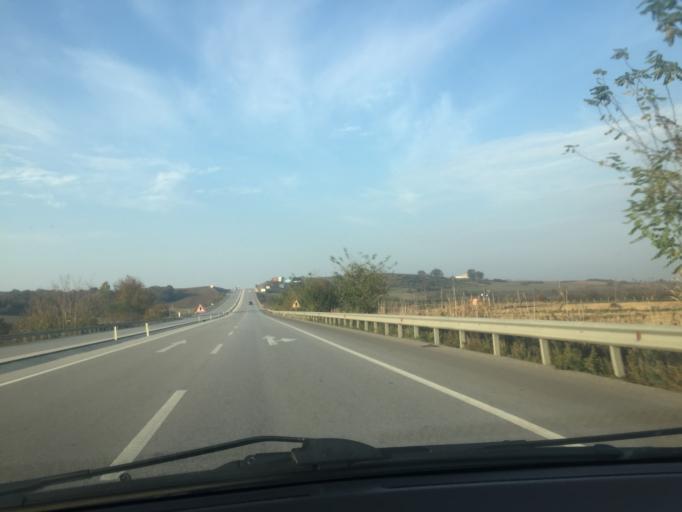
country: TR
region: Canakkale
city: Dimetoka
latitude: 40.2509
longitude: 27.3064
